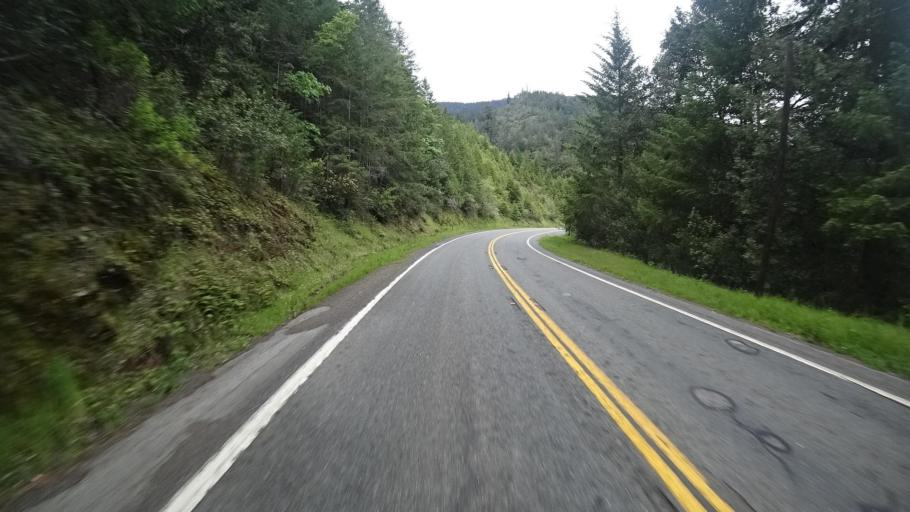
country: US
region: California
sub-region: Humboldt County
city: Willow Creek
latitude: 41.2268
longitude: -123.6577
